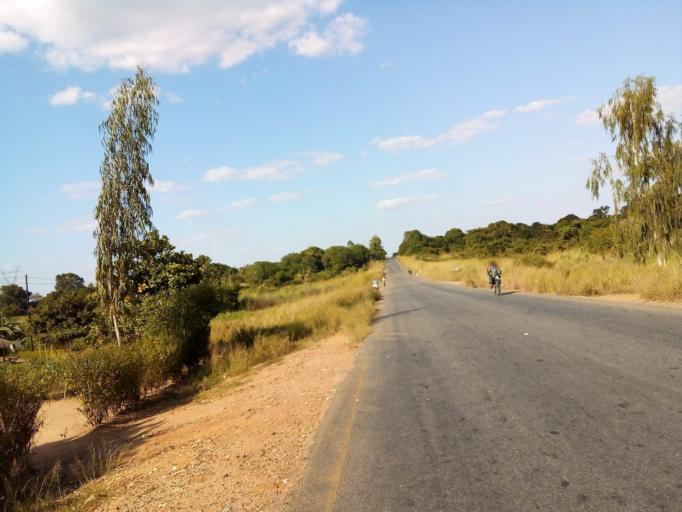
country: MZ
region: Zambezia
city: Quelimane
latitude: -17.5748
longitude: 36.6198
